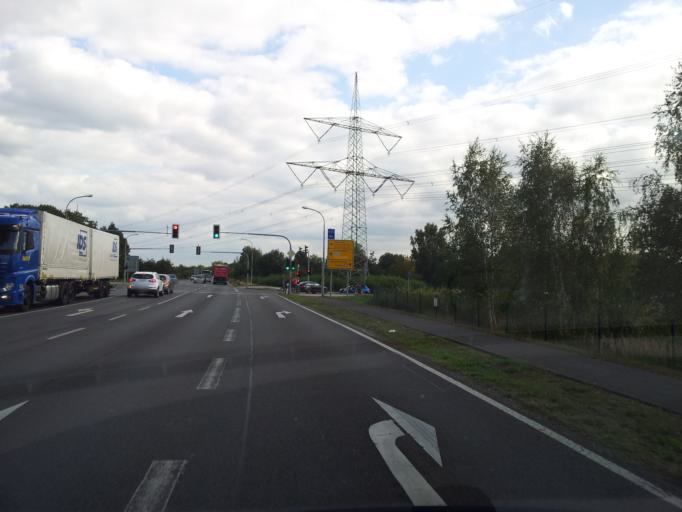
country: DE
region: Brandenburg
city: Ruhland
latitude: 51.4656
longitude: 13.8667
